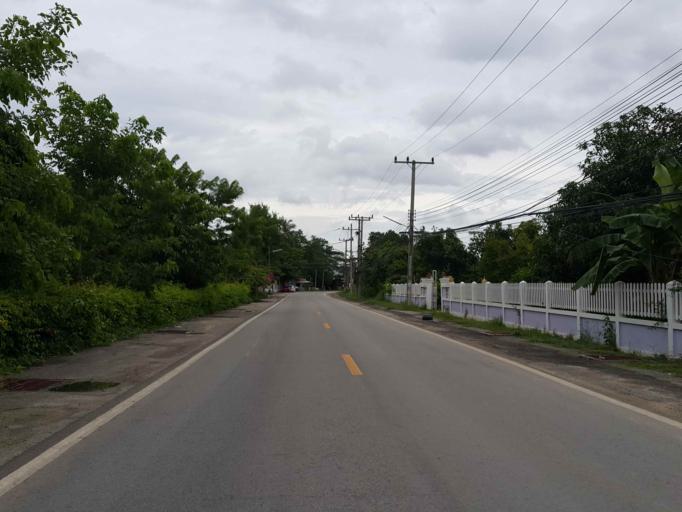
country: TH
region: Chiang Mai
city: San Sai
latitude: 18.8197
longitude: 99.0750
